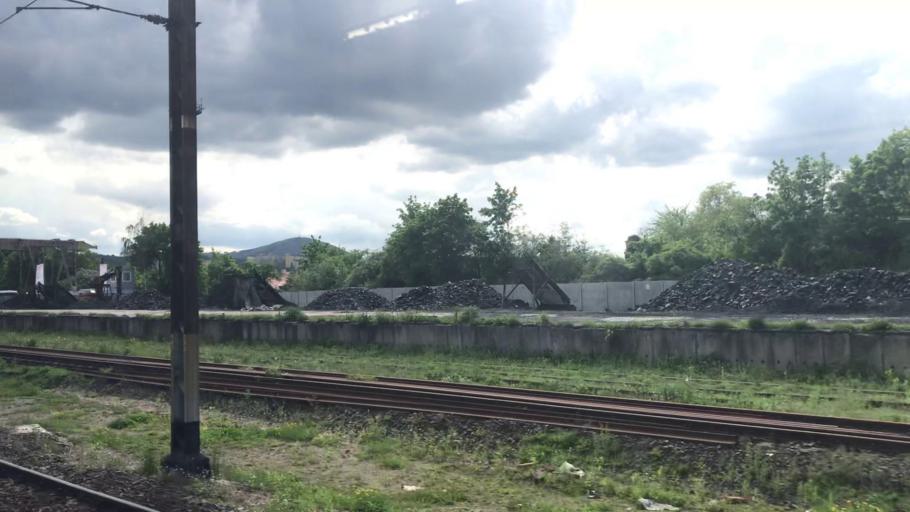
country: PL
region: Lower Silesian Voivodeship
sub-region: Powiat swidnicki
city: Swiebodzice
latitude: 50.8188
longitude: 16.3035
